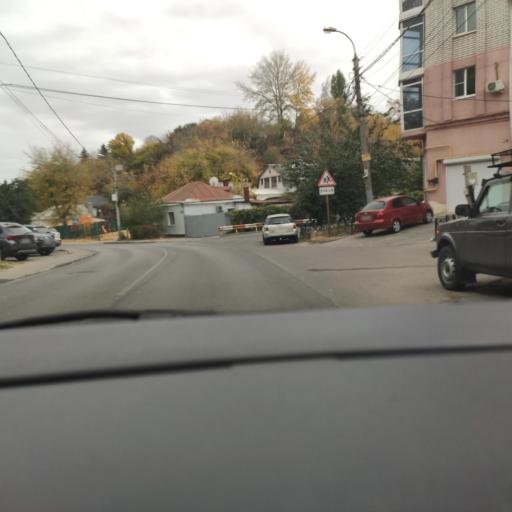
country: RU
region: Voronezj
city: Voronezh
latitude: 51.6530
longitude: 39.2022
